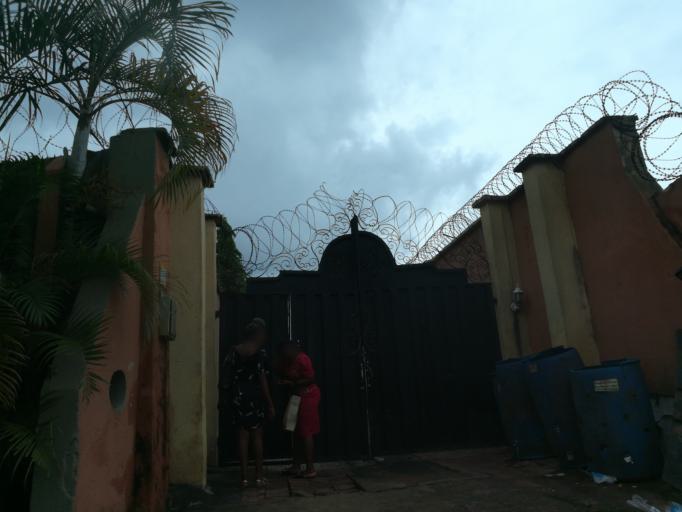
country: NG
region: Lagos
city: Agege
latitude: 6.6041
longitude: 3.3159
